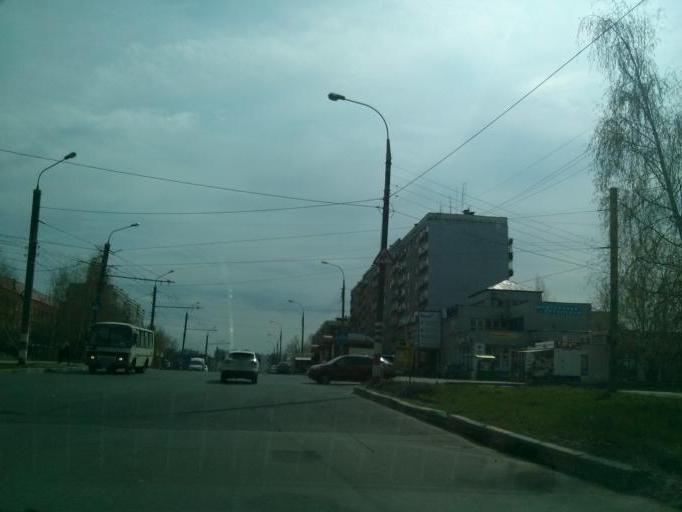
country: RU
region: Nizjnij Novgorod
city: Afonino
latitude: 56.2944
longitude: 44.0681
